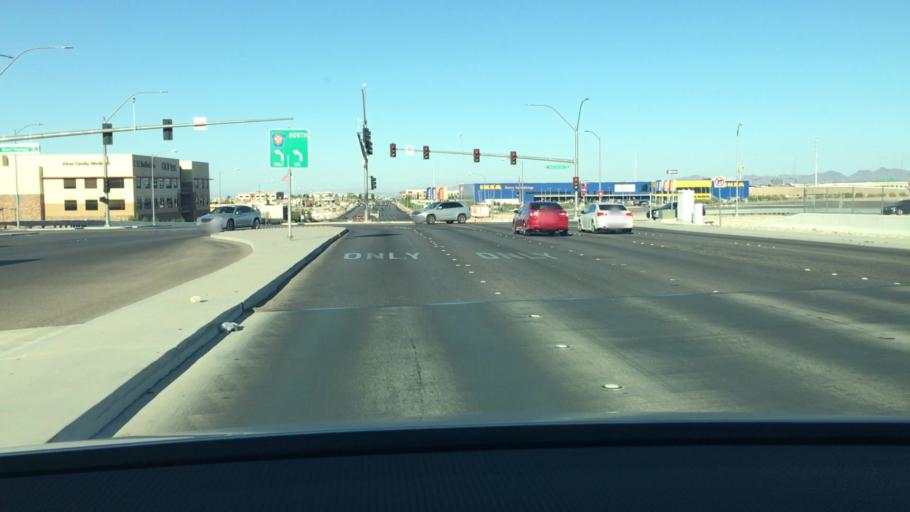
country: US
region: Nevada
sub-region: Clark County
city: Spring Valley
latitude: 36.0703
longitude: -115.2881
